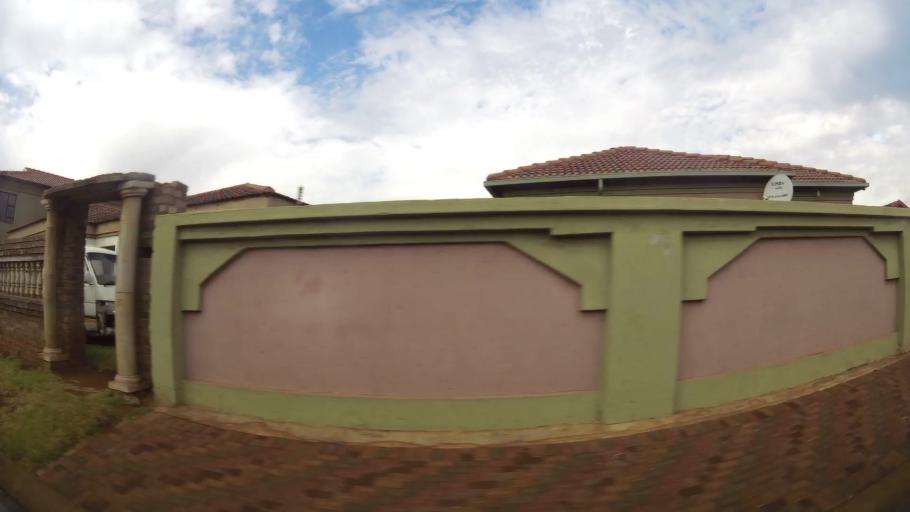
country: ZA
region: Gauteng
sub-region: Ekurhuleni Metropolitan Municipality
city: Germiston
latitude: -26.3325
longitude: 28.1927
